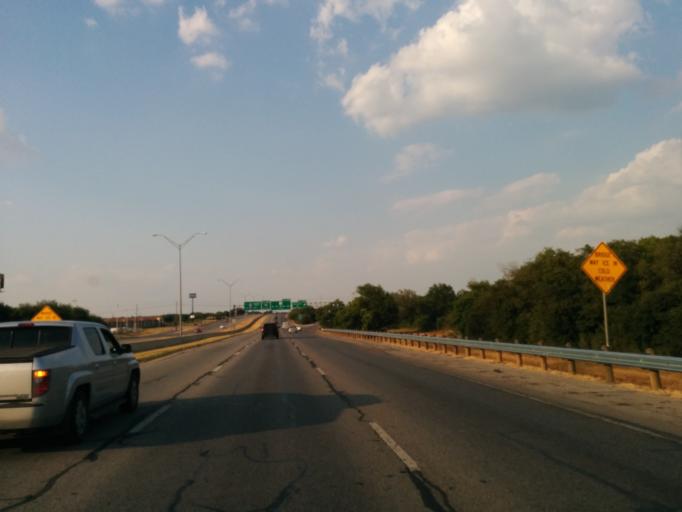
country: US
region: Texas
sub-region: Bexar County
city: Kirby
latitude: 29.4202
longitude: -98.4248
